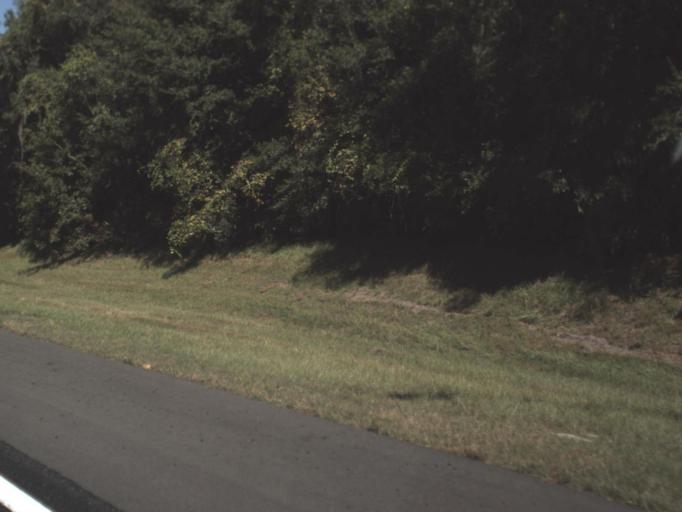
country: US
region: Florida
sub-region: Citrus County
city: Sugarmill Woods
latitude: 28.6459
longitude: -82.4909
